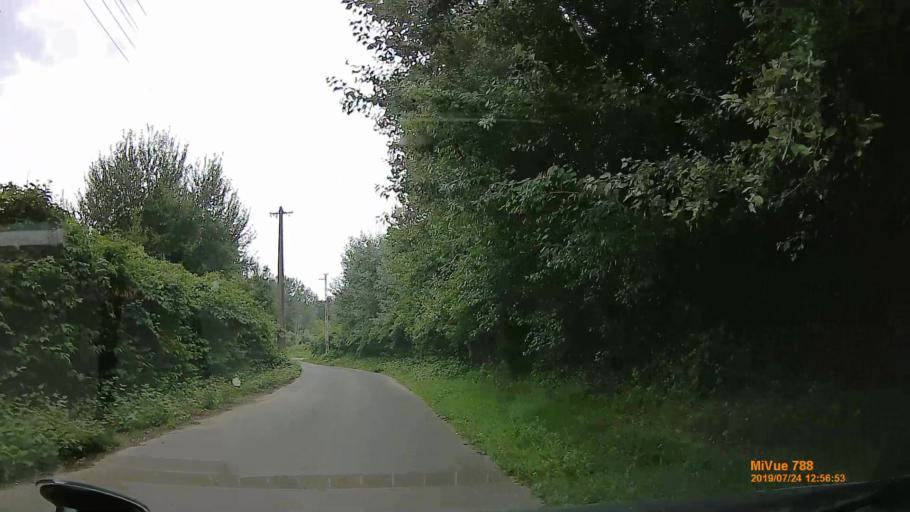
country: HU
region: Szabolcs-Szatmar-Bereg
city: Aranyosapati
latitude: 48.2210
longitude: 22.2811
